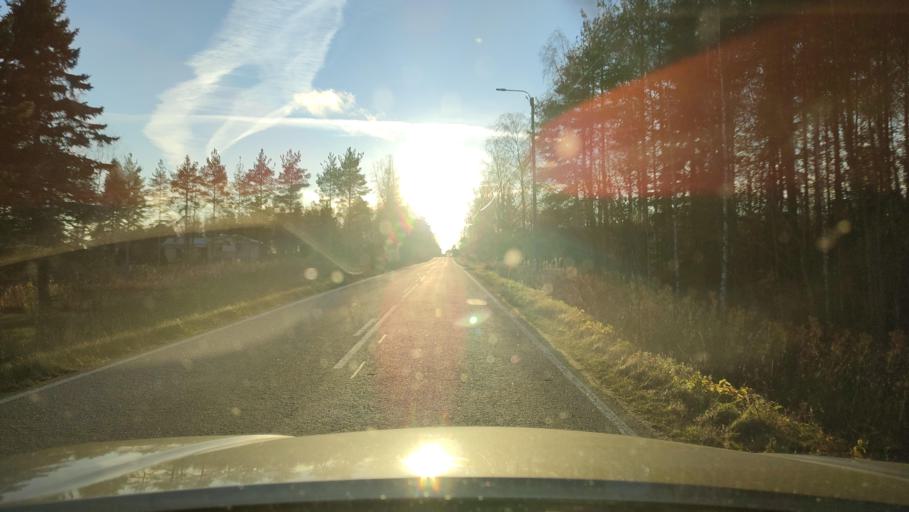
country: FI
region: Ostrobothnia
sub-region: Vaasa
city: Malax
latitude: 62.7064
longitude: 21.6001
